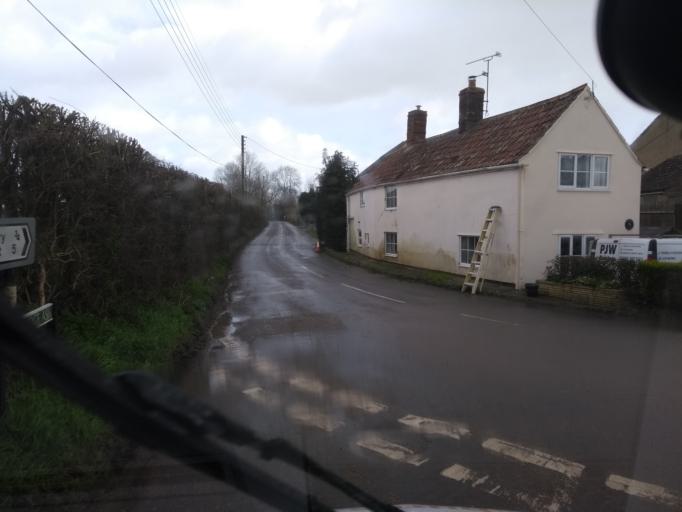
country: GB
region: England
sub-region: Somerset
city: South Petherton
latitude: 50.9807
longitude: -2.8202
